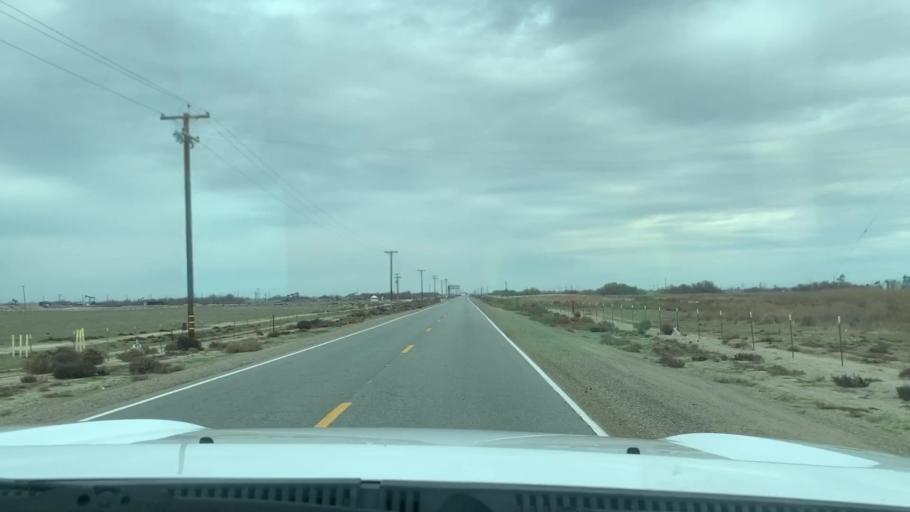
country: US
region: California
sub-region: Kern County
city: Rosedale
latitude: 35.3141
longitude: -119.2524
